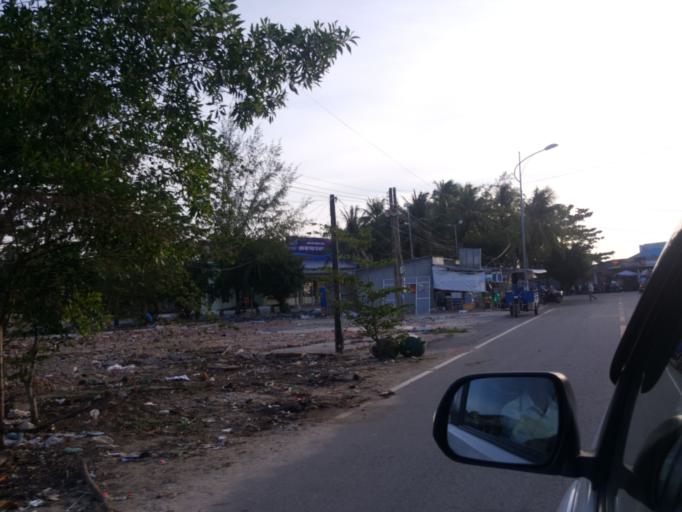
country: VN
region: Kien Giang
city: Duong GJong
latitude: 10.1494
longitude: 104.0367
